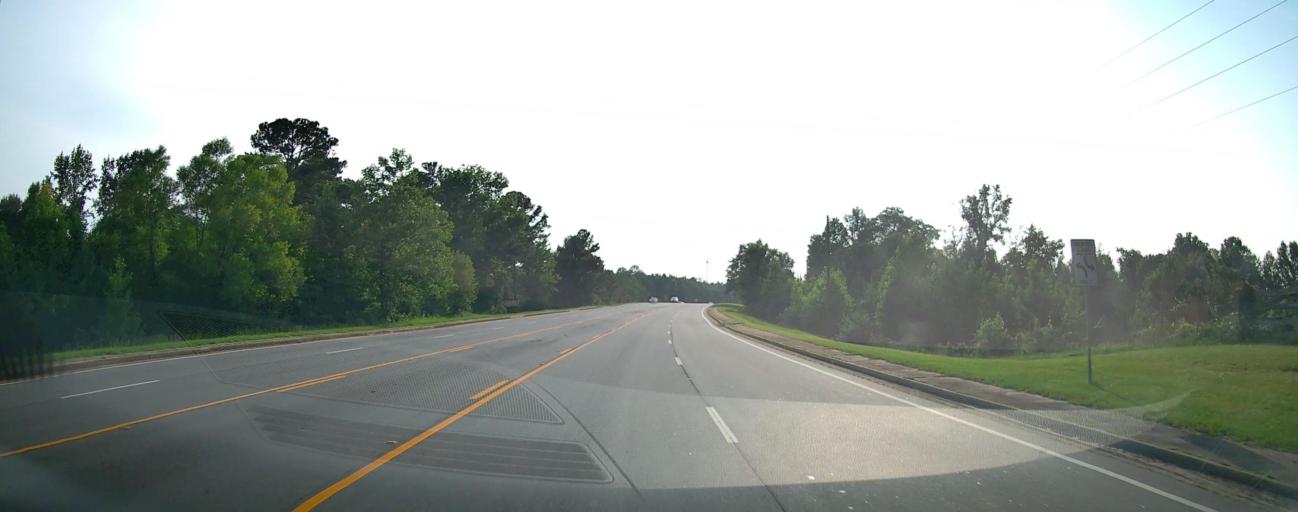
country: US
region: Georgia
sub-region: Talbot County
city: Talbotton
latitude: 32.5750
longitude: -84.5619
